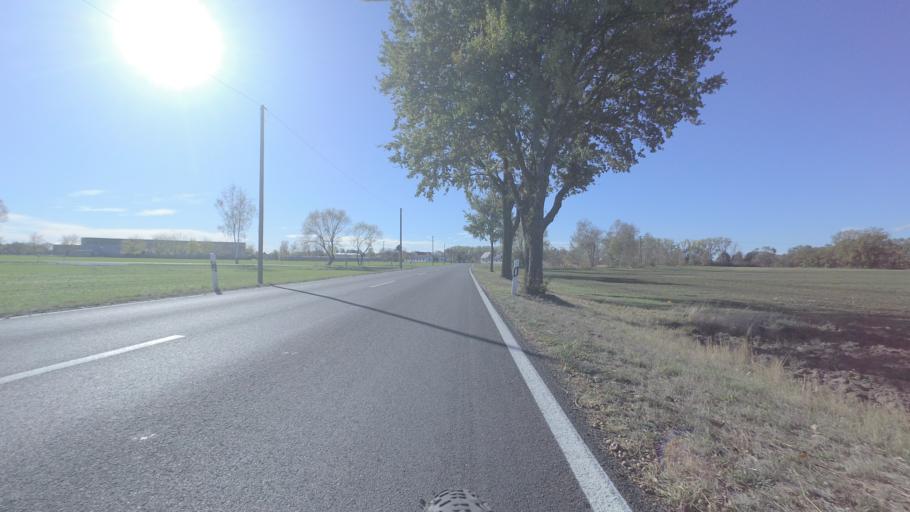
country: DE
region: Saxony
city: Nauwalde
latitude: 51.4468
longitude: 13.4549
